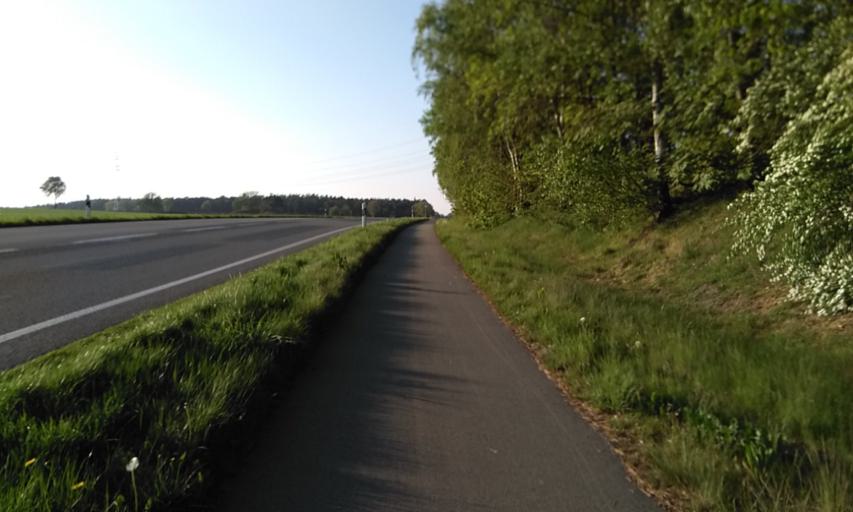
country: DE
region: Lower Saxony
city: Dollern
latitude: 53.5219
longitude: 9.5593
